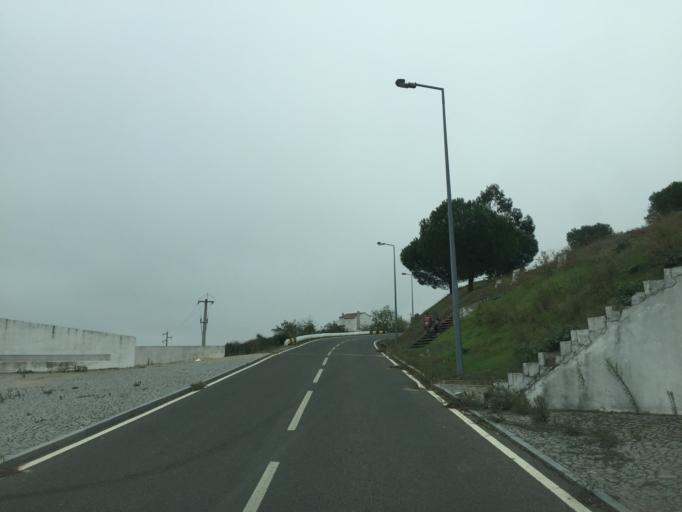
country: PT
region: Portalegre
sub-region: Arronches
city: Arronches
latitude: 39.0548
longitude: -7.4401
